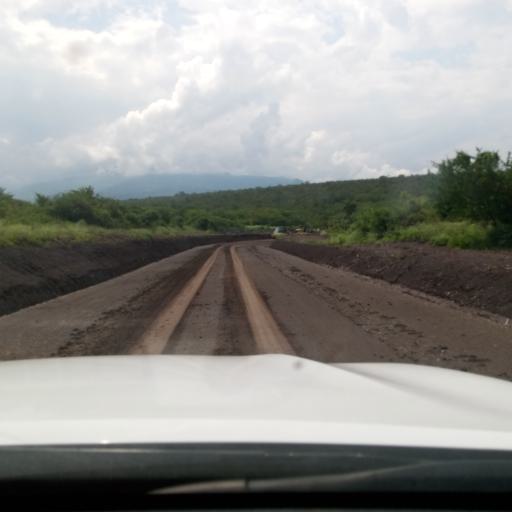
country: ET
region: Southern Nations, Nationalities, and People's Region
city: Arba Minch'
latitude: 6.3615
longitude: 37.2968
